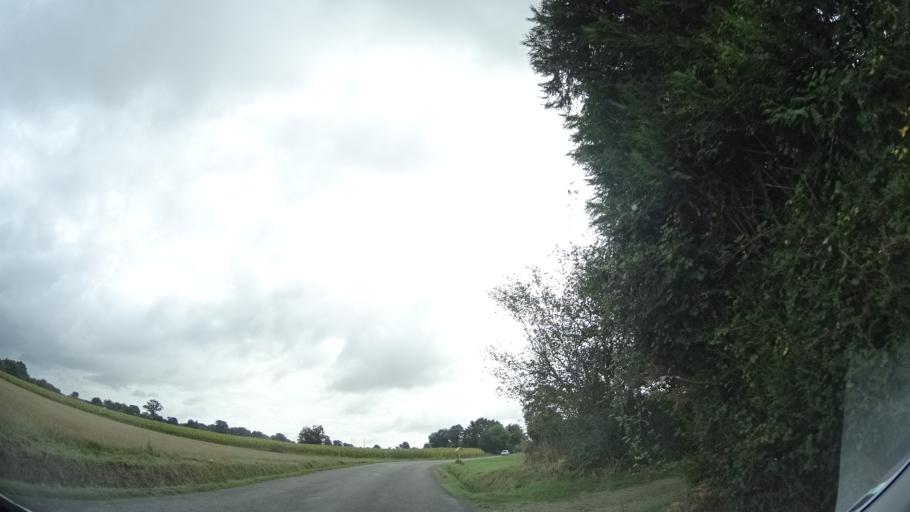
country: FR
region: Brittany
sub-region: Departement d'Ille-et-Vilaine
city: Montreuil-sur-Ille
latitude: 48.3025
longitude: -1.6577
